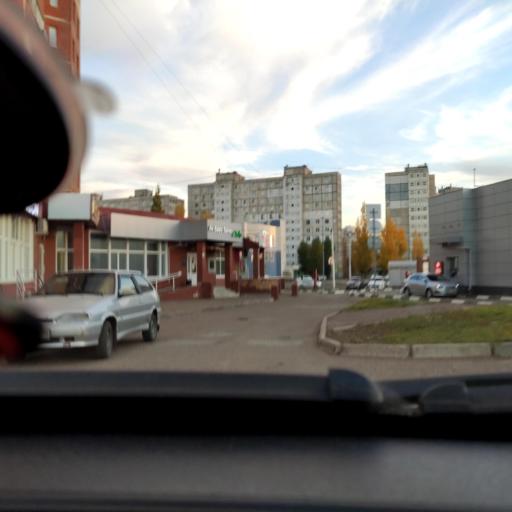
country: RU
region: Bashkortostan
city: Ufa
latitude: 54.7747
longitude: 56.0673
